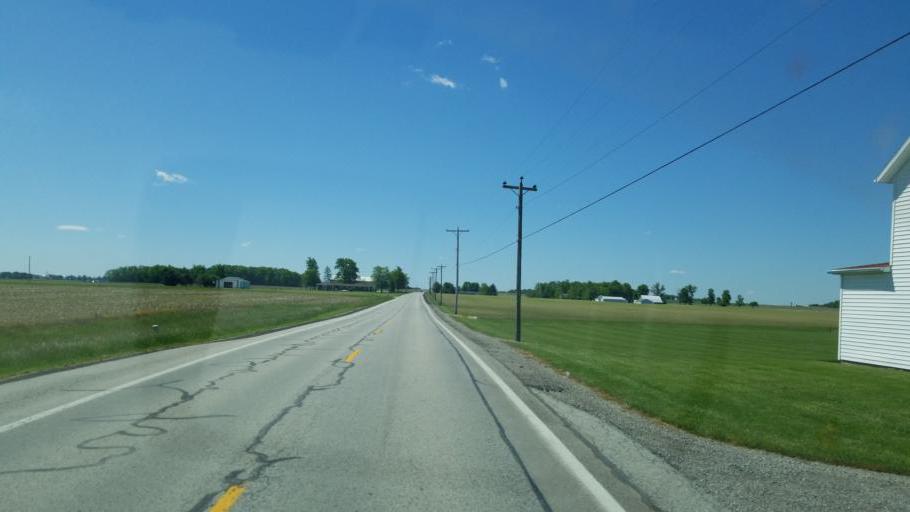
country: US
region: Ohio
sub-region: Shelby County
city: Jackson Center
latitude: 40.4030
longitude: -84.0406
